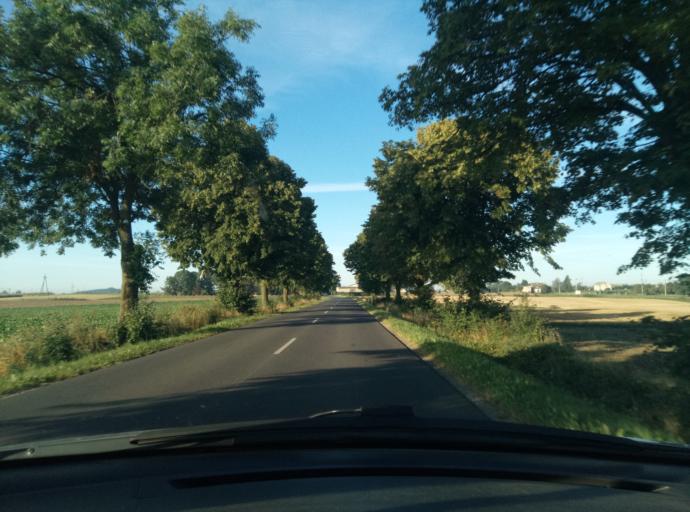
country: PL
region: Kujawsko-Pomorskie
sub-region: Powiat golubsko-dobrzynski
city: Kowalewo Pomorskie
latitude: 53.2064
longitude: 18.9208
